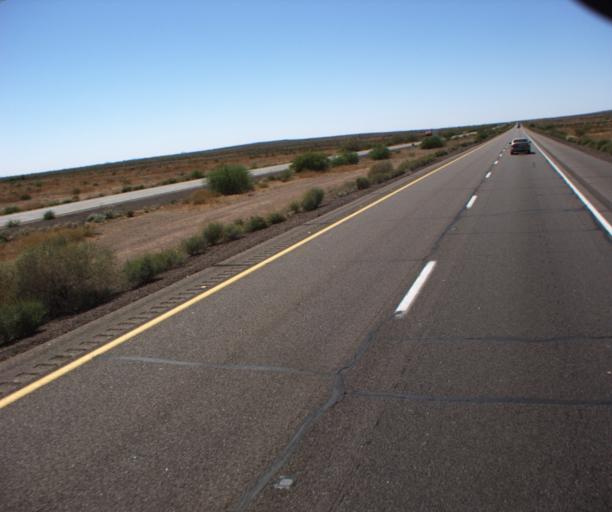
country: US
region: Arizona
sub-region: Maricopa County
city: Gila Bend
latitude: 32.8849
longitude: -113.0883
